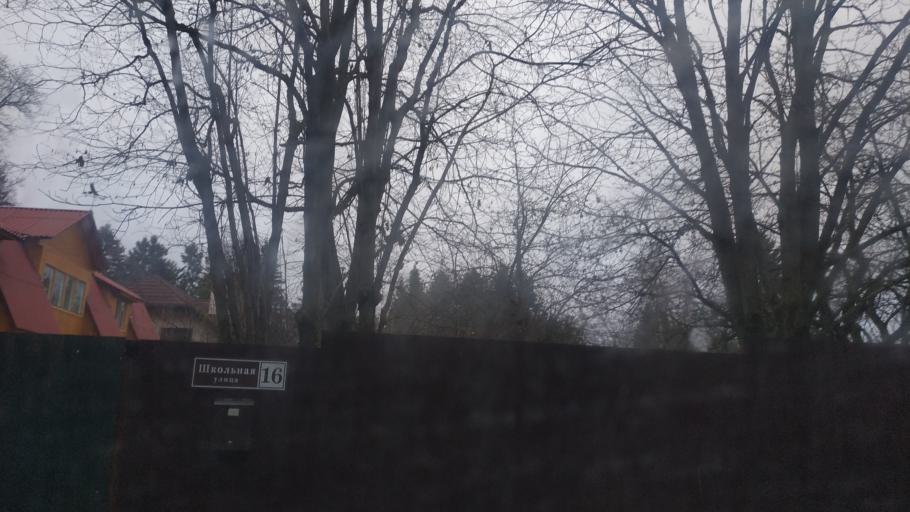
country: RU
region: Moskovskaya
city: Lugovaya
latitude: 56.0564
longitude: 37.4761
